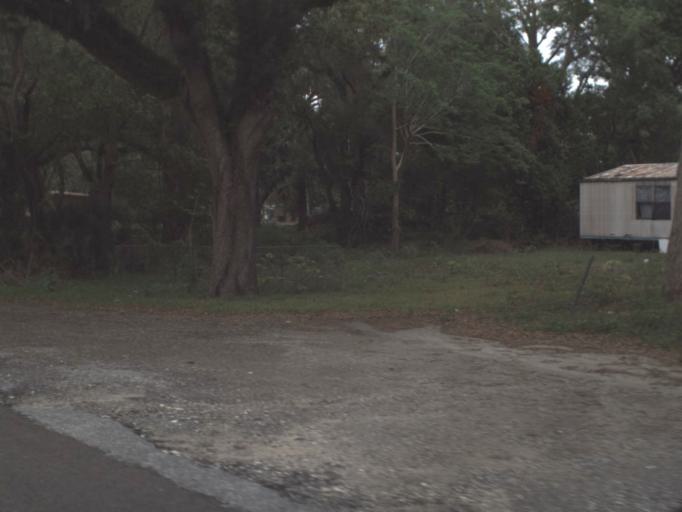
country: US
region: Florida
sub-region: Lake County
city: Umatilla
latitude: 28.9975
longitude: -81.6422
